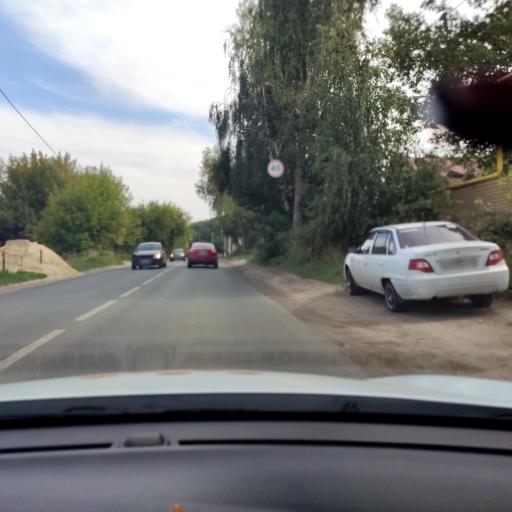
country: RU
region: Tatarstan
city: Staroye Arakchino
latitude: 55.7999
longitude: 48.9802
